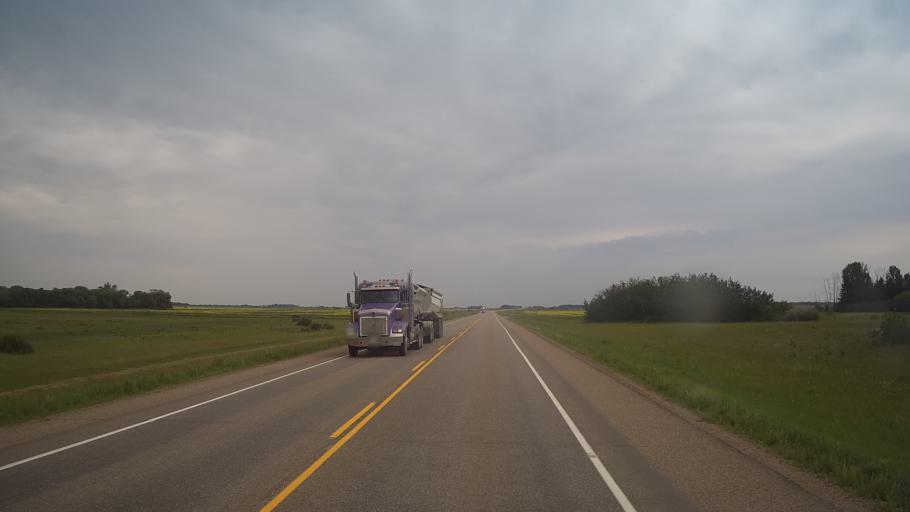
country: CA
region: Saskatchewan
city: Langham
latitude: 52.1285
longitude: -107.2378
